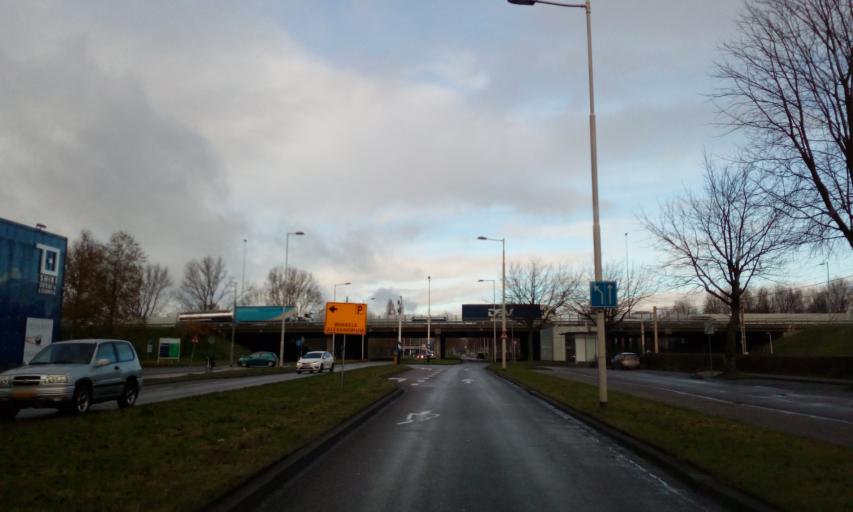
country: NL
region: South Holland
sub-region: Gemeente Rotterdam
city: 's-Gravenland
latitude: 51.9524
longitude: 4.5511
